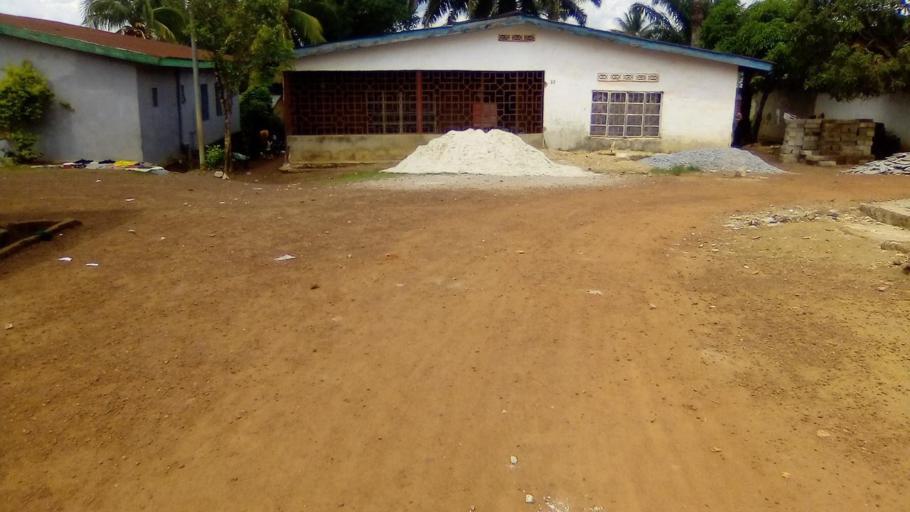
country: SL
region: Southern Province
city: Bo
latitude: 7.9605
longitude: -11.7215
